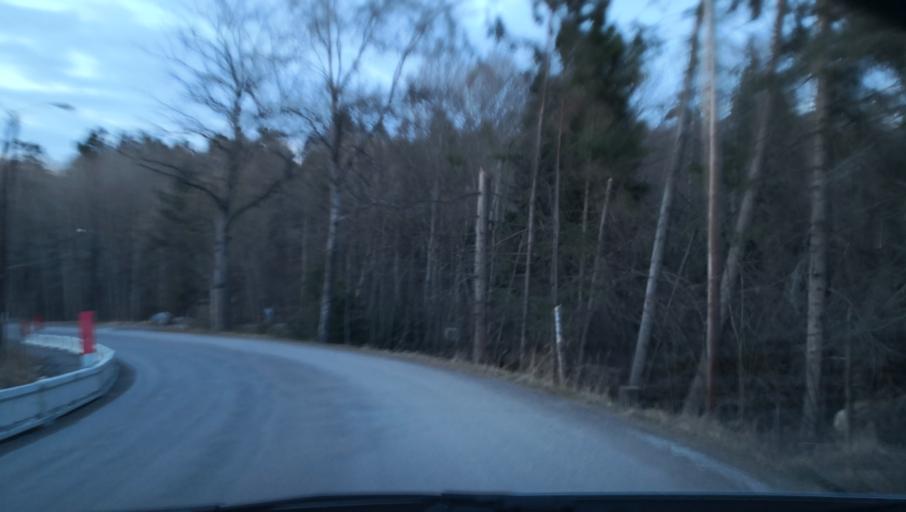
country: SE
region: Stockholm
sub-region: Nacka Kommun
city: Kummelnas
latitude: 59.3541
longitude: 18.2966
